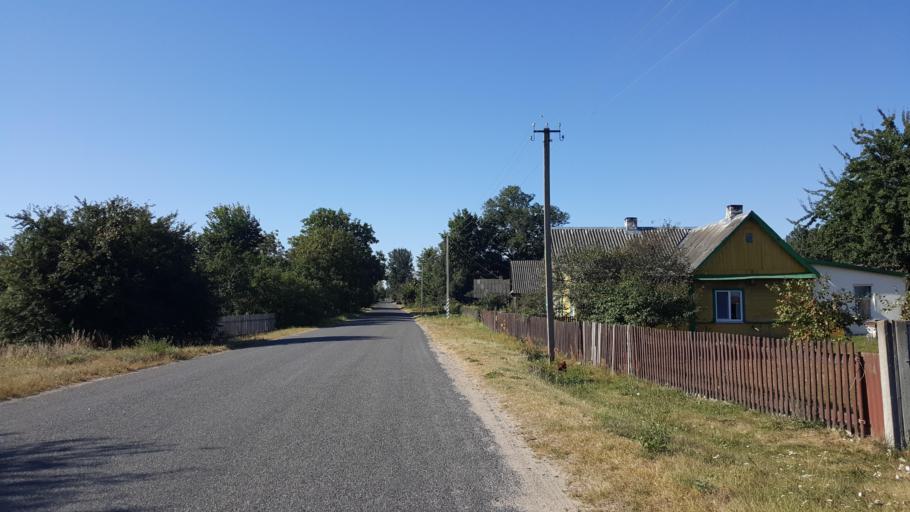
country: BY
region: Brest
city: Kamyanyets
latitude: 52.3834
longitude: 23.7450
